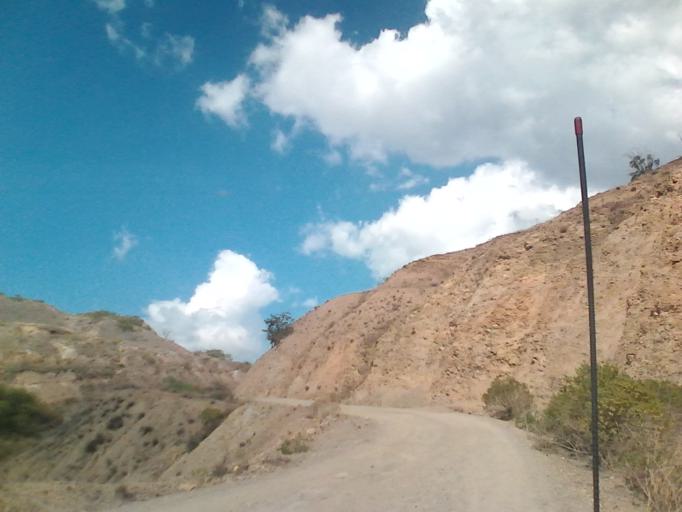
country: CO
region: Boyaca
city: Sachica
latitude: 5.5770
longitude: -73.5165
